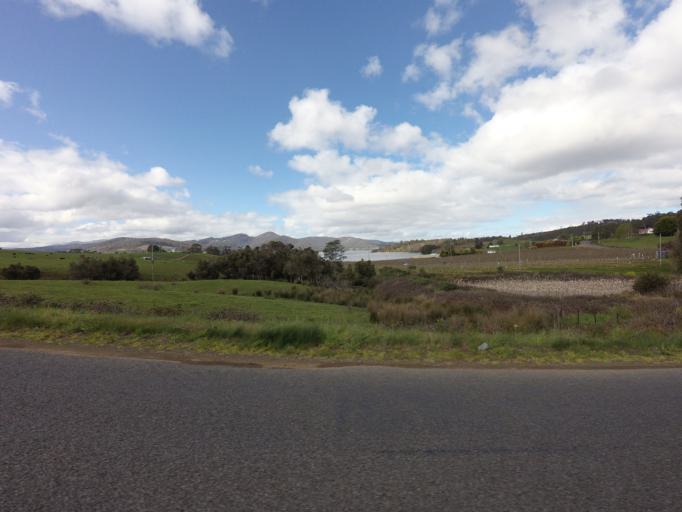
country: AU
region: Tasmania
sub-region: Huon Valley
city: Geeveston
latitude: -43.2034
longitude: 146.9652
